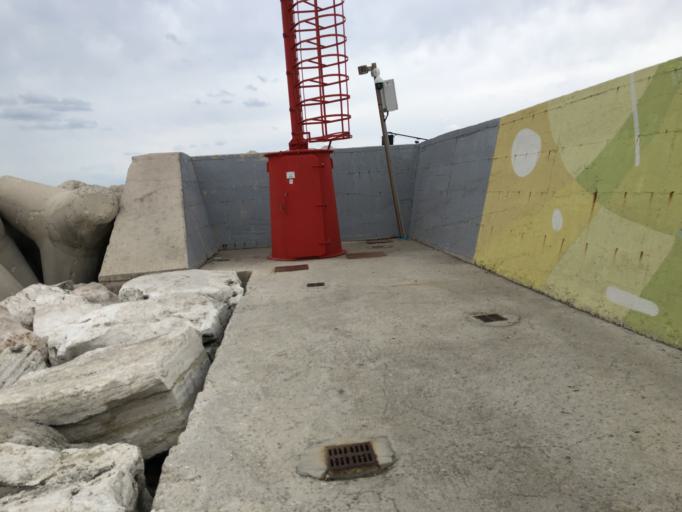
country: IT
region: The Marches
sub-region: Provincia di Pesaro e Urbino
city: Pesaro
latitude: 43.9276
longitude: 12.9057
